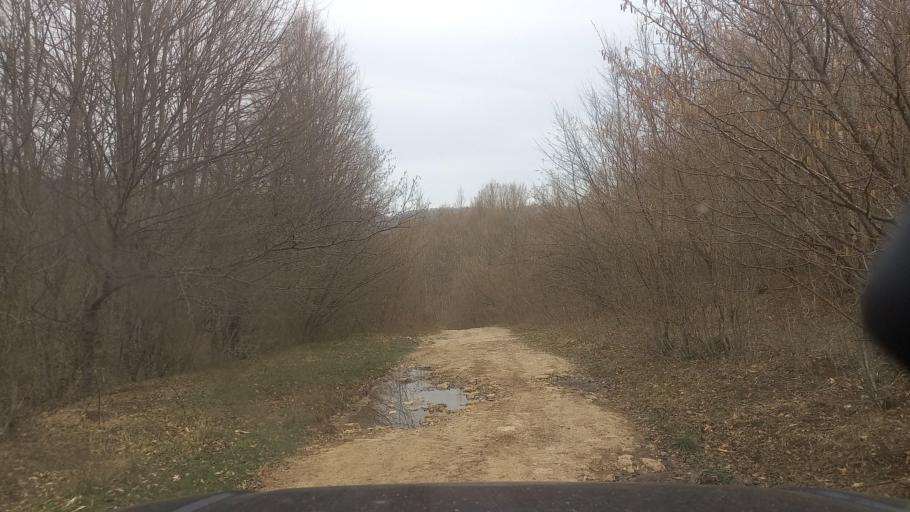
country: RU
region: Adygeya
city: Kamennomostskiy
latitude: 44.1919
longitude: 39.9671
